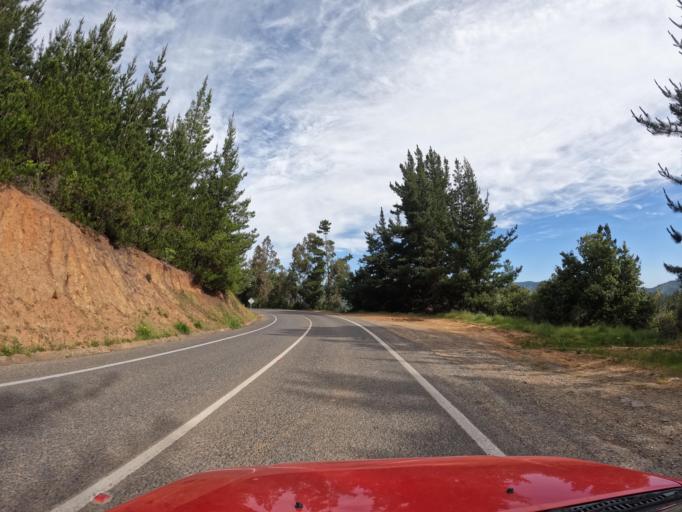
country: CL
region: Maule
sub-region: Provincia de Talca
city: Talca
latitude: -35.2949
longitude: -71.9729
